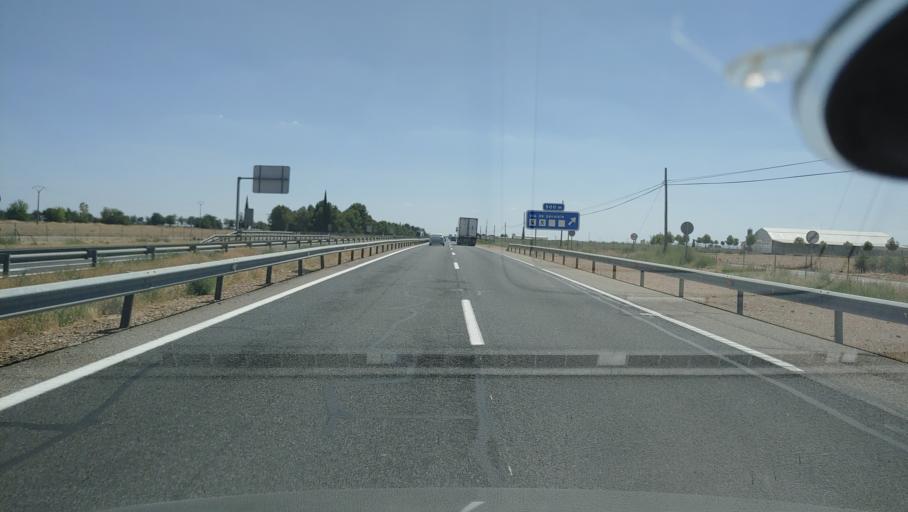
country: ES
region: Castille-La Mancha
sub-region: Provincia de Ciudad Real
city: Manzanares
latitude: 39.1213
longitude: -3.3778
